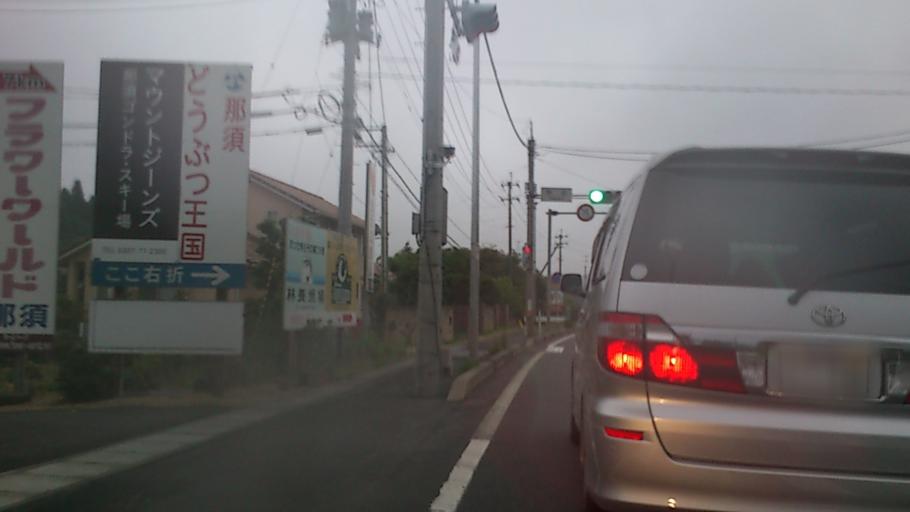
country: JP
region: Tochigi
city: Kuroiso
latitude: 37.1117
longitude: 140.1471
